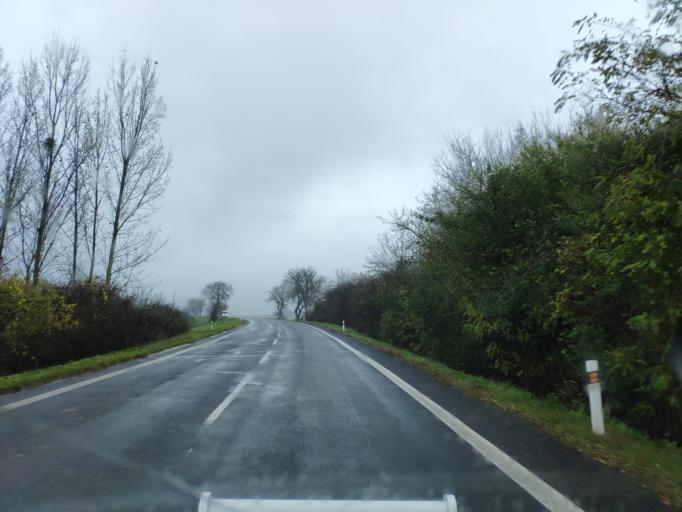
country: SK
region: Kosicky
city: Cierna nad Tisou
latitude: 48.4456
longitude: 21.9888
